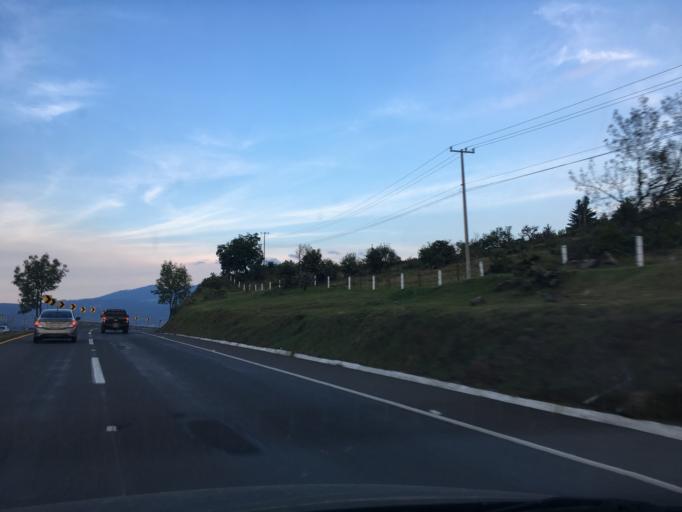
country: MX
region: Michoacan
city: Huiramba
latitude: 19.5511
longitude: -101.4311
